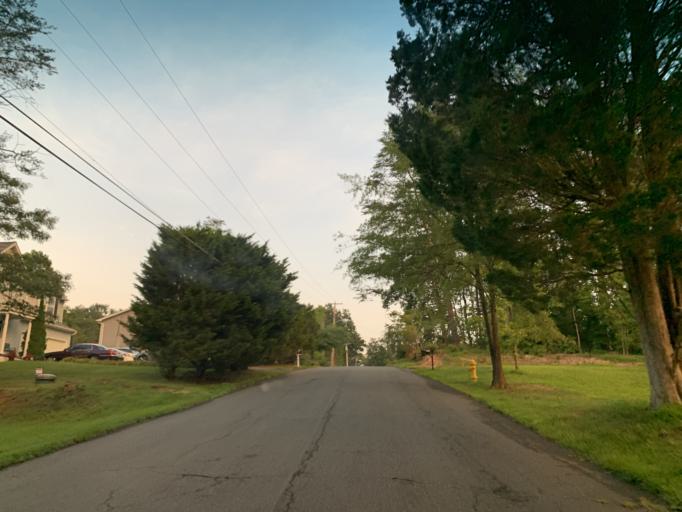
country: US
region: Maryland
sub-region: Harford County
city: Edgewood
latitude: 39.4154
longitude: -76.3368
